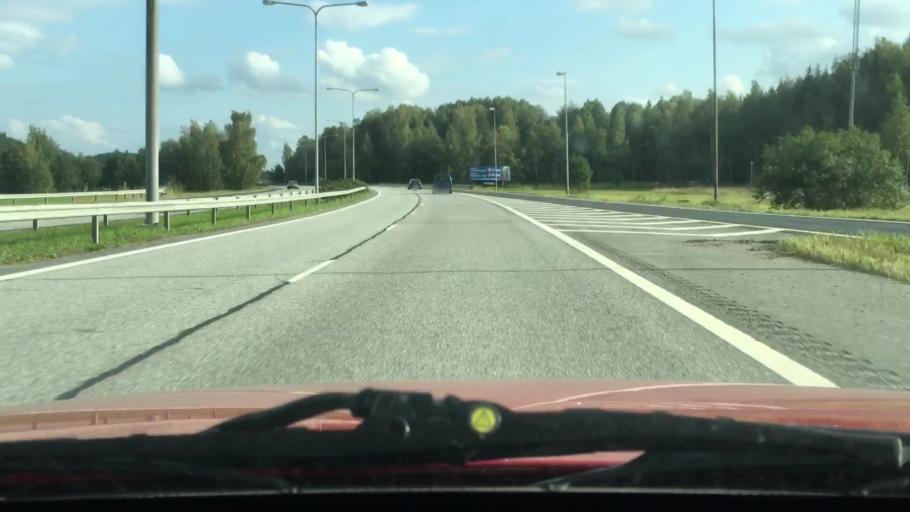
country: FI
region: Varsinais-Suomi
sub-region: Turku
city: Raisio
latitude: 60.4804
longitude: 22.1823
